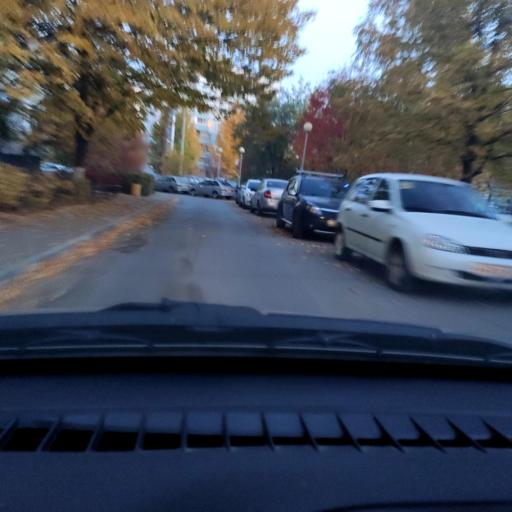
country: RU
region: Samara
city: Tol'yatti
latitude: 53.5457
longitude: 49.3402
